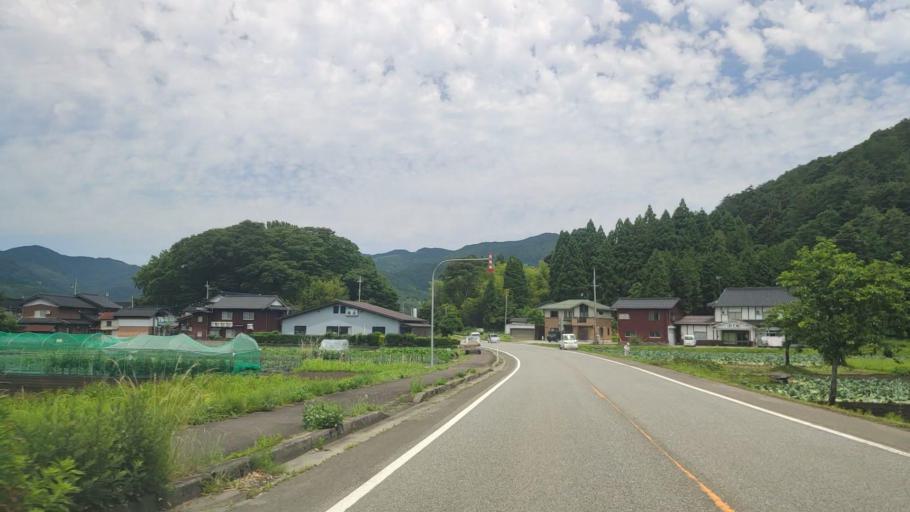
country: JP
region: Hyogo
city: Toyooka
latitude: 35.5013
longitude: 134.6728
